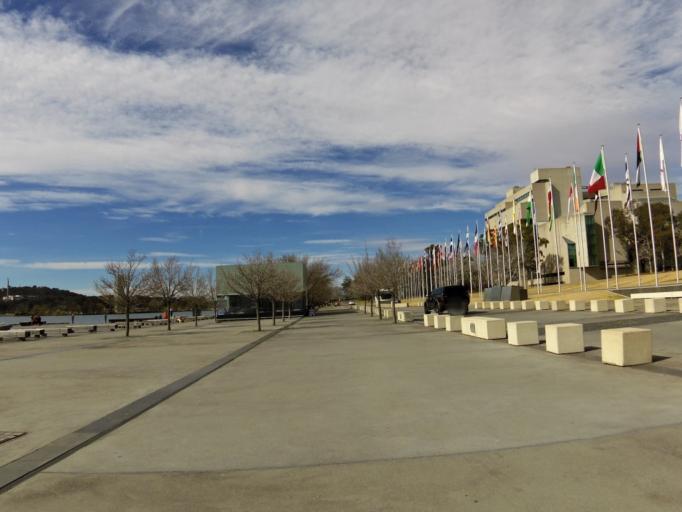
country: AU
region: Australian Capital Territory
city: Canberra
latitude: -35.2972
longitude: 149.1347
